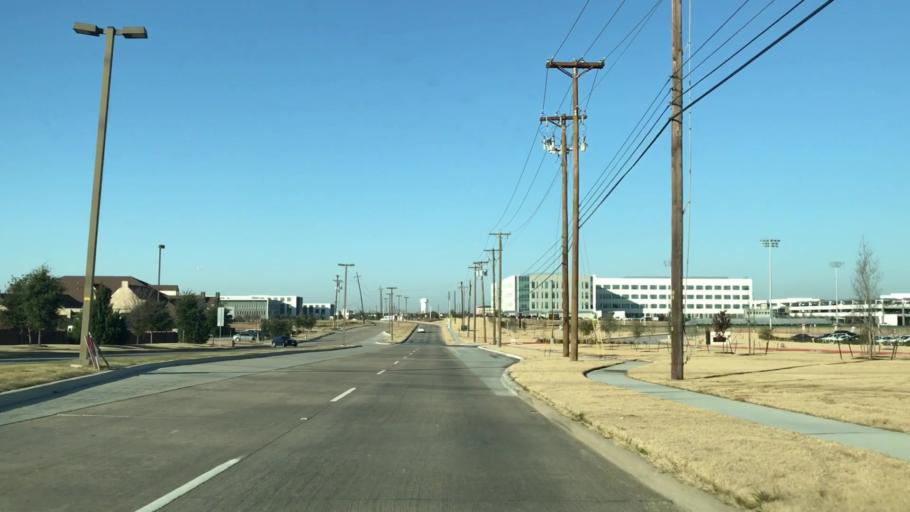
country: US
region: Texas
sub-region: Dallas County
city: Coppell
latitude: 32.9258
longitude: -96.9807
